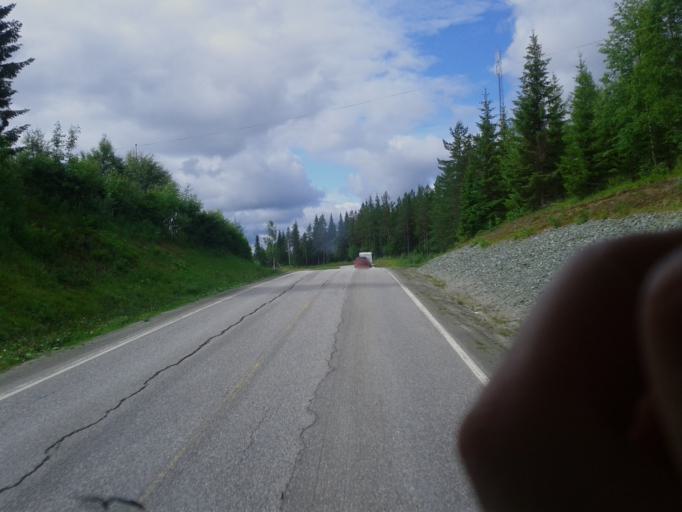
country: NO
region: Nord-Trondelag
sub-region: Hoylandet
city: Hoylandet
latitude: 64.6333
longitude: 12.6100
